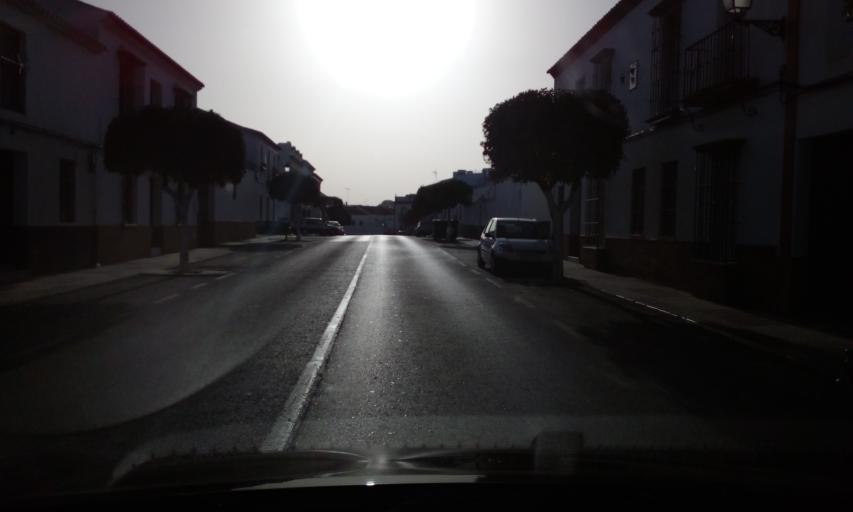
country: ES
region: Andalusia
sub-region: Provincia de Sevilla
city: Olivares
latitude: 37.4168
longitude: -6.1548
